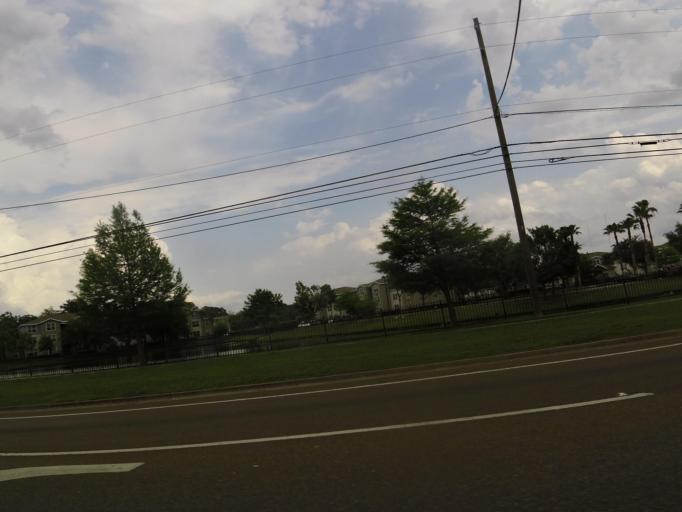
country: US
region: Florida
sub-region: Duval County
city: Jacksonville
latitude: 30.3030
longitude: -81.7459
